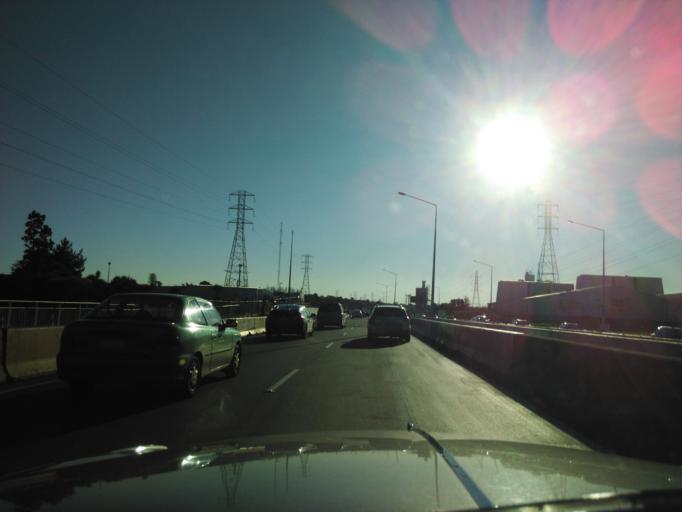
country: NZ
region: Auckland
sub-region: Auckland
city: Rosebank
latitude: -36.8528
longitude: 174.6408
